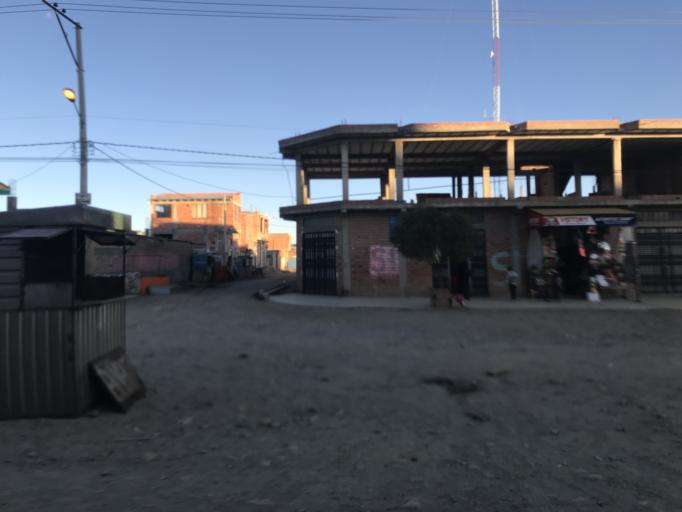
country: BO
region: La Paz
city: La Paz
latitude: -16.5037
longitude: -68.2473
